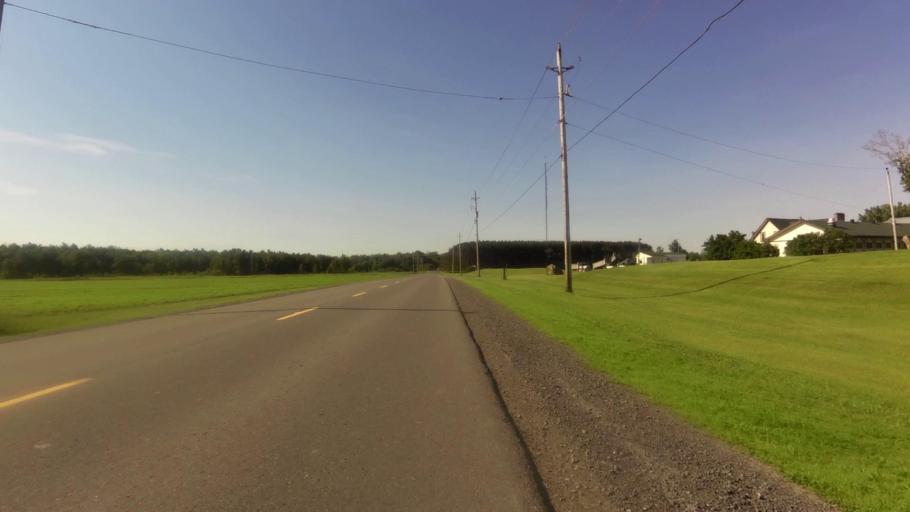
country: CA
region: Ontario
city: Ottawa
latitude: 45.2267
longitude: -75.5609
